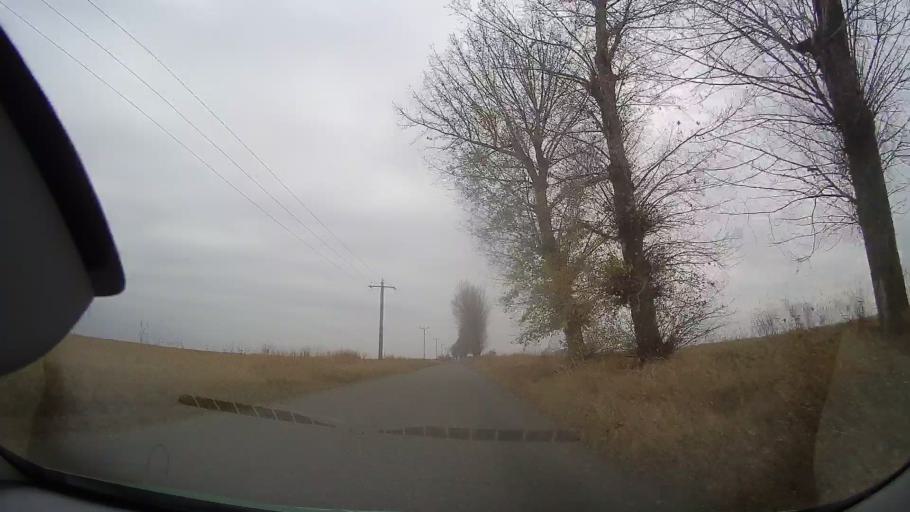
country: RO
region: Buzau
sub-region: Comuna Pogoanele
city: Pogoanele
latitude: 44.9483
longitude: 27.0123
